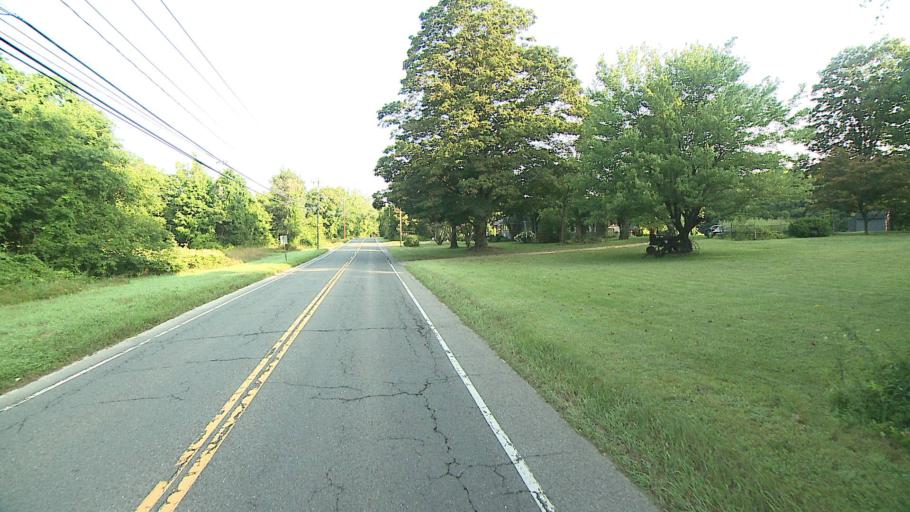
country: US
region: Connecticut
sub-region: Litchfield County
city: New Milford
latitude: 41.5899
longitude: -73.4484
